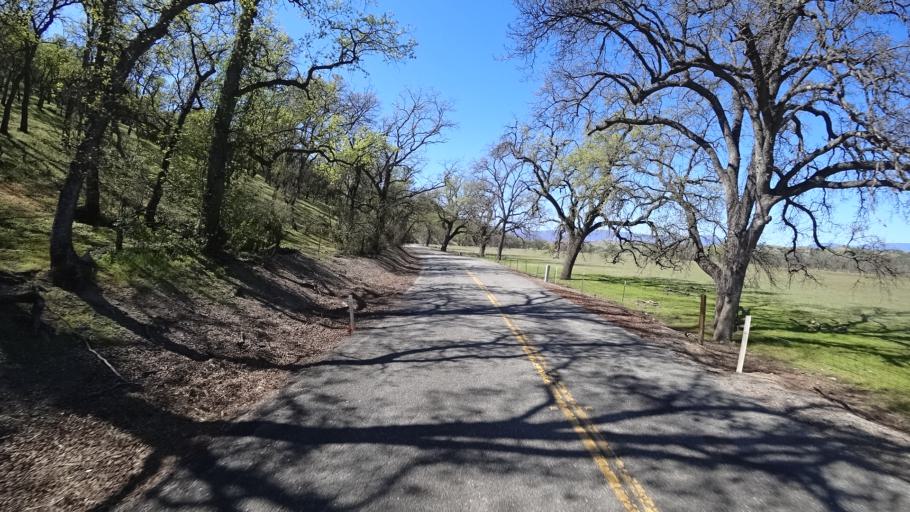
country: US
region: California
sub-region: Tehama County
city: Rancho Tehama Reserve
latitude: 39.7971
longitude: -122.4359
